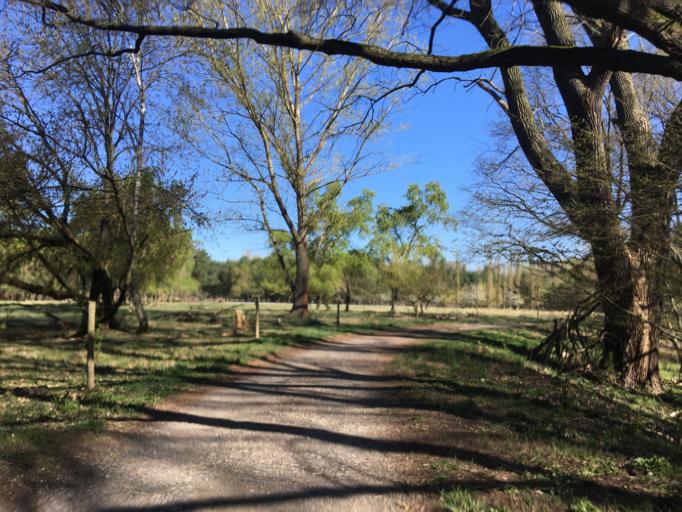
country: DE
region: Berlin
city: Buch
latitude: 52.6389
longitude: 13.4656
